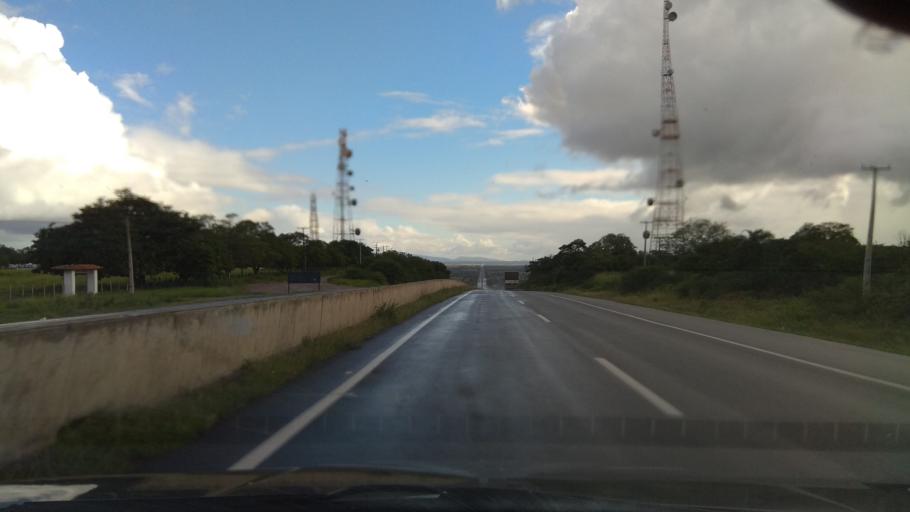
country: BR
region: Bahia
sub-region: Santo Estevao
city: Santo Estevao
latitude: -12.4668
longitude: -39.2834
